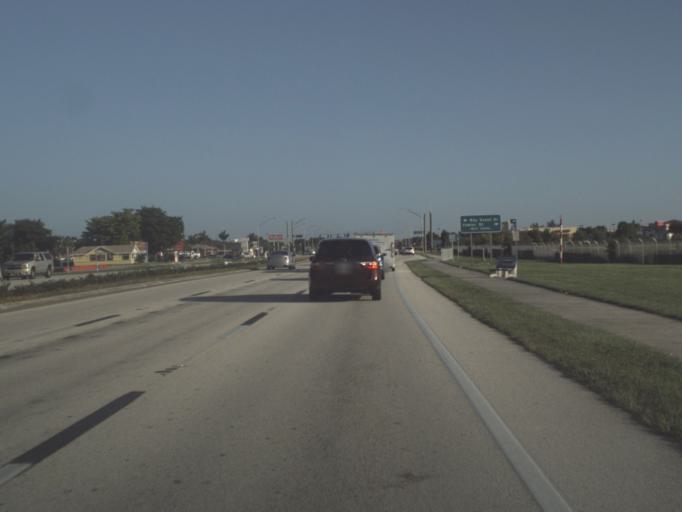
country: US
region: Florida
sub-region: Lee County
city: Pine Manor
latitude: 26.5798
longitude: -81.8718
